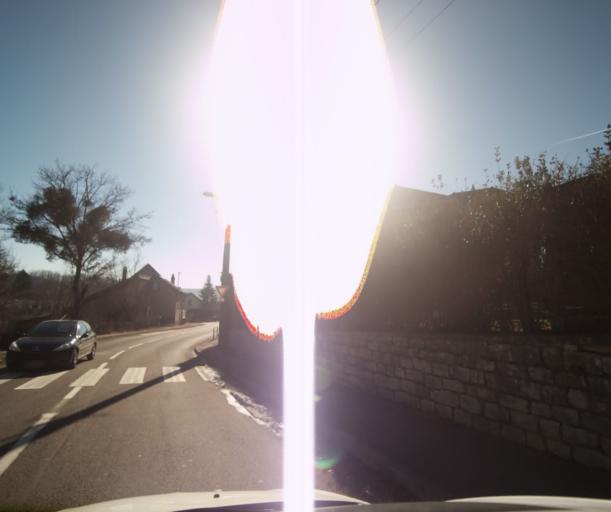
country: FR
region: Franche-Comte
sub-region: Departement du Doubs
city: Thise
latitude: 47.2671
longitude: 6.0499
